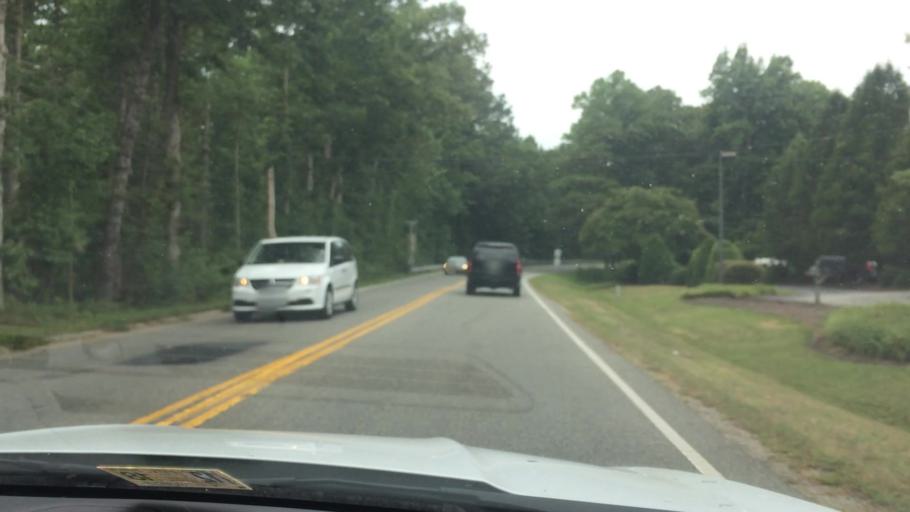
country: US
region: Virginia
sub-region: James City County
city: Williamsburg
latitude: 37.3131
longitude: -76.7724
